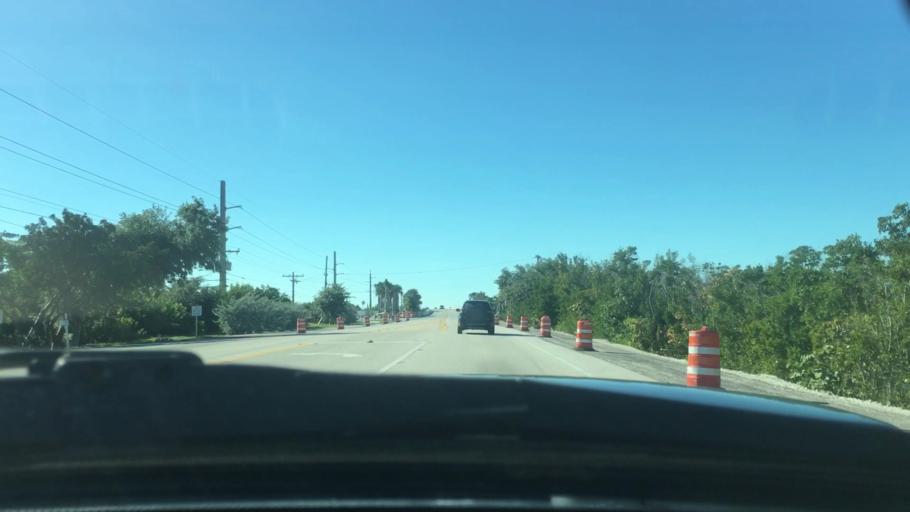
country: US
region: Florida
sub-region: Monroe County
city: Cudjoe Key
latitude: 24.6632
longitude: -81.4617
